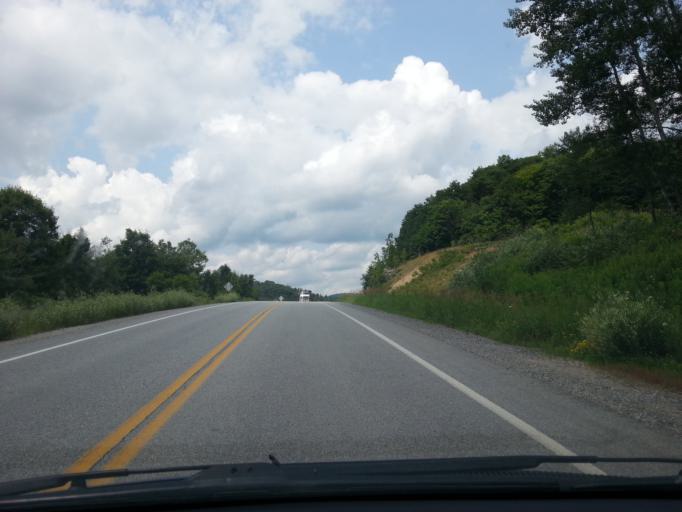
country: CA
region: Quebec
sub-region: Outaouais
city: Val-des-Monts
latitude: 45.6581
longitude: -75.7155
